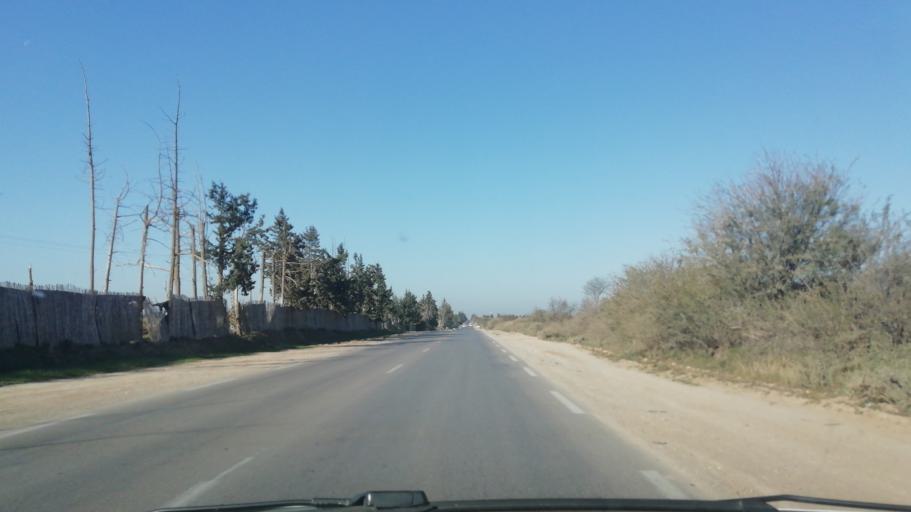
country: DZ
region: Mascara
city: Sig
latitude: 35.5695
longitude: -0.0484
